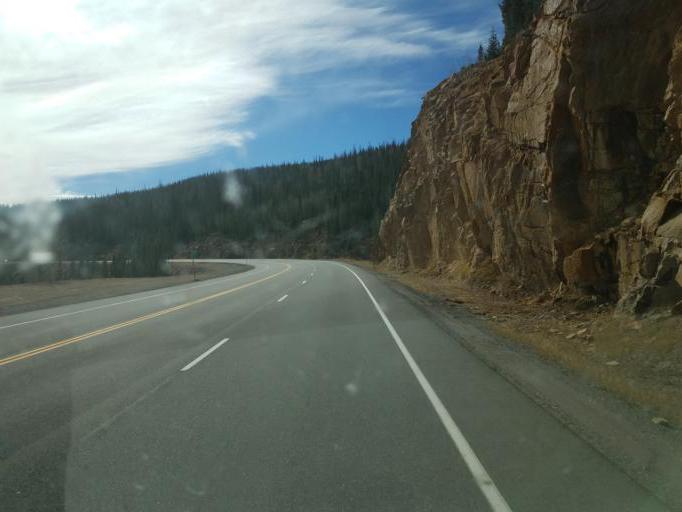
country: US
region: Colorado
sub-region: Archuleta County
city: Pagosa Springs
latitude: 37.5073
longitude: -106.7738
